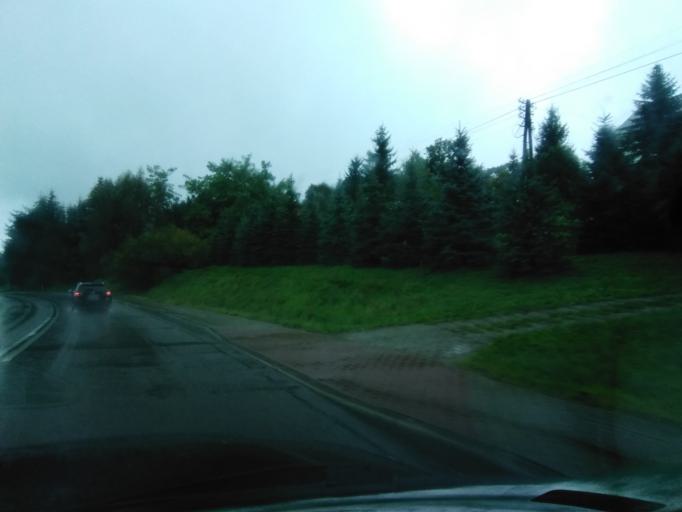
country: PL
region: Subcarpathian Voivodeship
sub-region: Powiat ropczycko-sedziszowski
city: Niedzwiada
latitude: 50.0136
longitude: 21.5521
